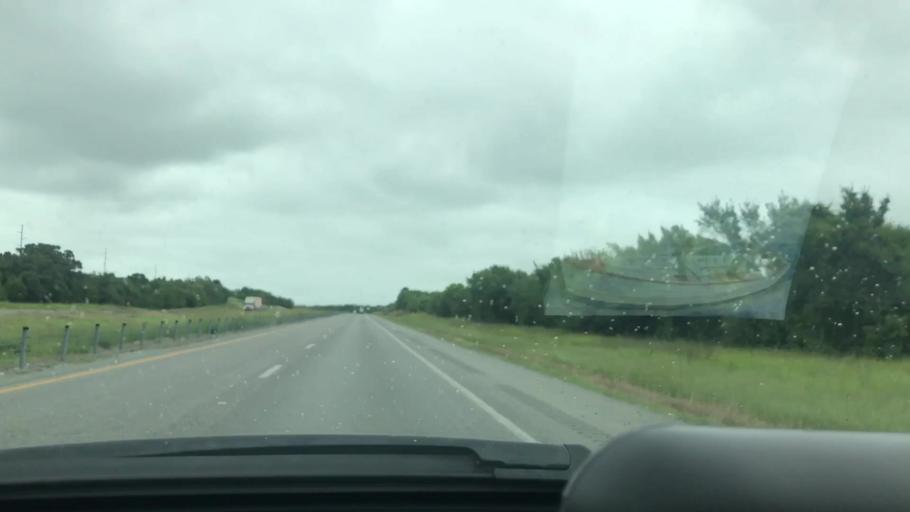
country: US
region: Oklahoma
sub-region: Coal County
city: Coalgate
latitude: 34.6400
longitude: -95.9498
